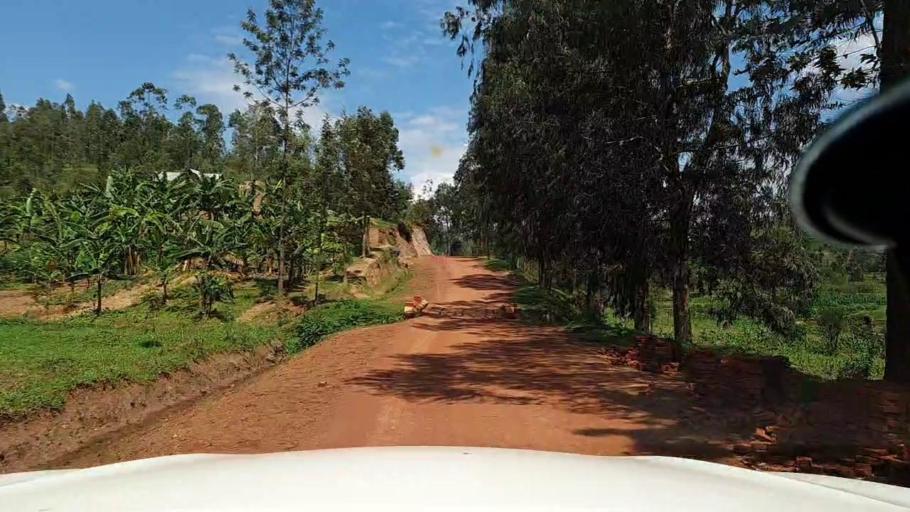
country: RW
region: Kigali
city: Kigali
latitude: -1.7814
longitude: 29.8789
